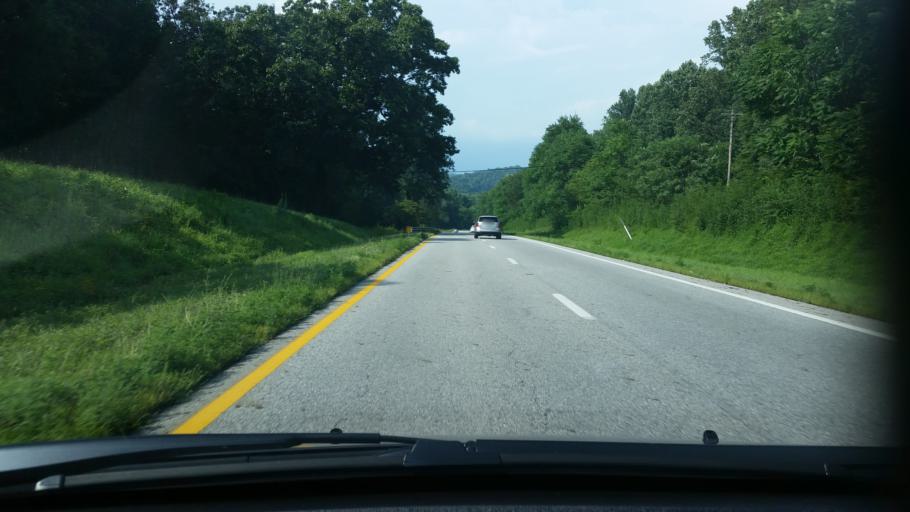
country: US
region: Virginia
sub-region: Nelson County
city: Lovingston
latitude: 37.7343
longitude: -78.8925
